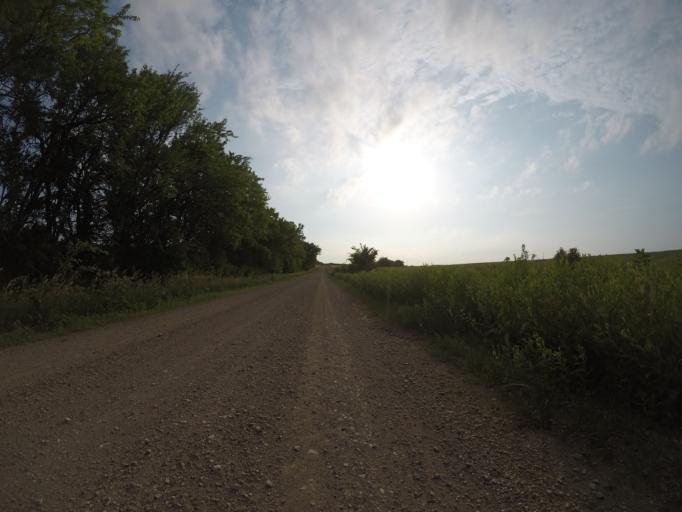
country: US
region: Kansas
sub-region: Wabaunsee County
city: Alma
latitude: 39.1015
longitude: -96.3559
